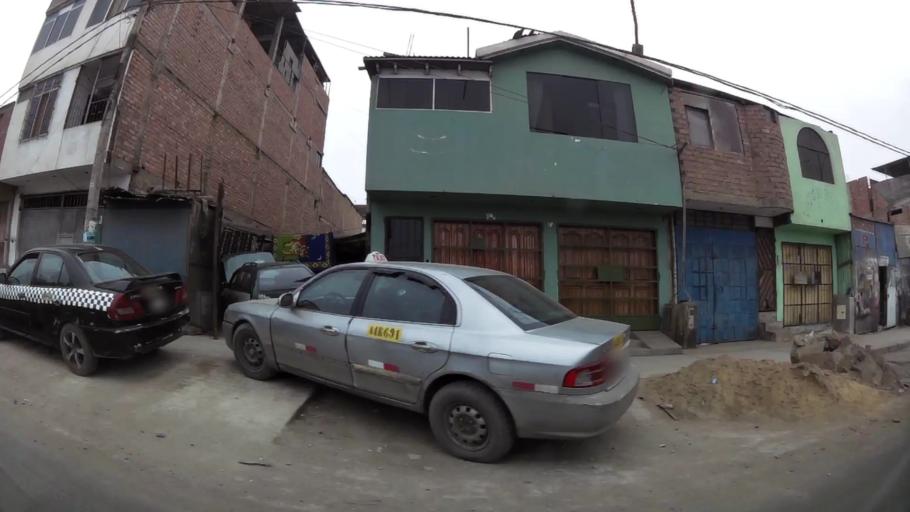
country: PE
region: Lima
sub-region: Lima
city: Punta Hermosa
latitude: -12.2419
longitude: -76.9162
